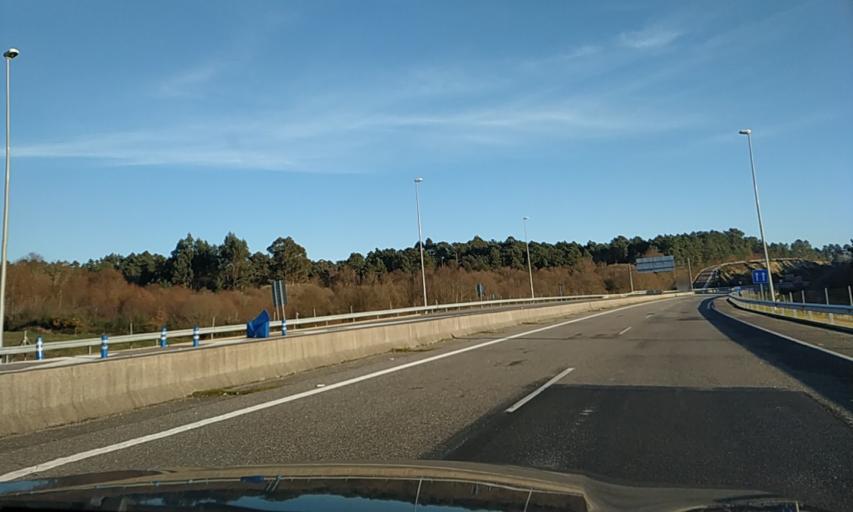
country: ES
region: Galicia
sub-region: Provincia de Ourense
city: Maside
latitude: 42.4475
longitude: -8.0214
